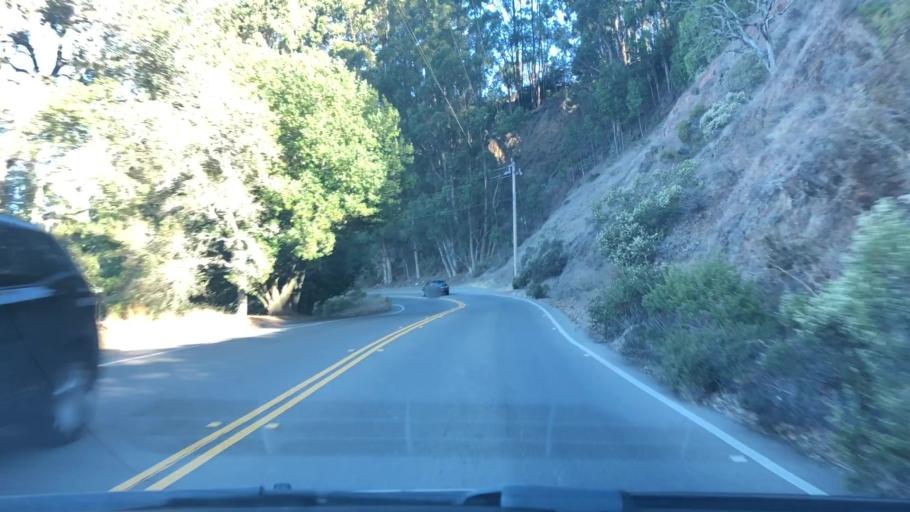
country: US
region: California
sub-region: Contra Costa County
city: Orinda
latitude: 37.8731
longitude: -122.2208
